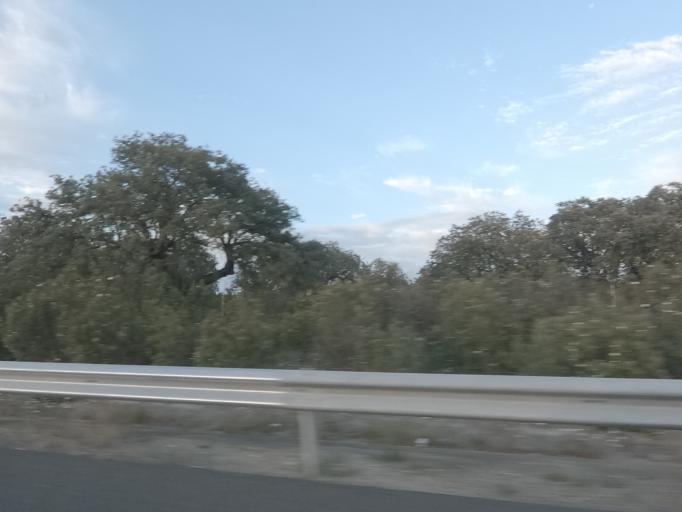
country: ES
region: Extremadura
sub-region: Provincia de Caceres
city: Casas de Don Antonio
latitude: 39.1979
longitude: -6.2797
